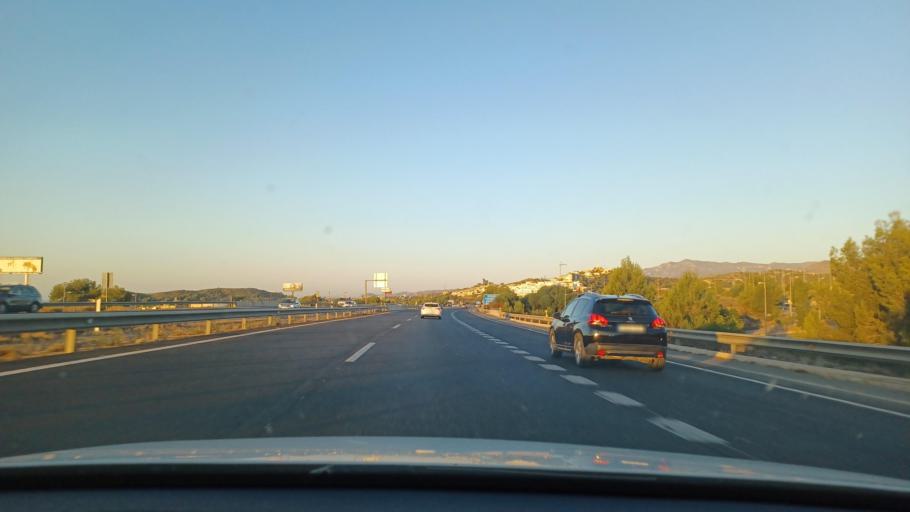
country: ES
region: Valencia
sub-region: Provincia de Alicante
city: Benidorm
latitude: 38.5426
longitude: -0.1745
